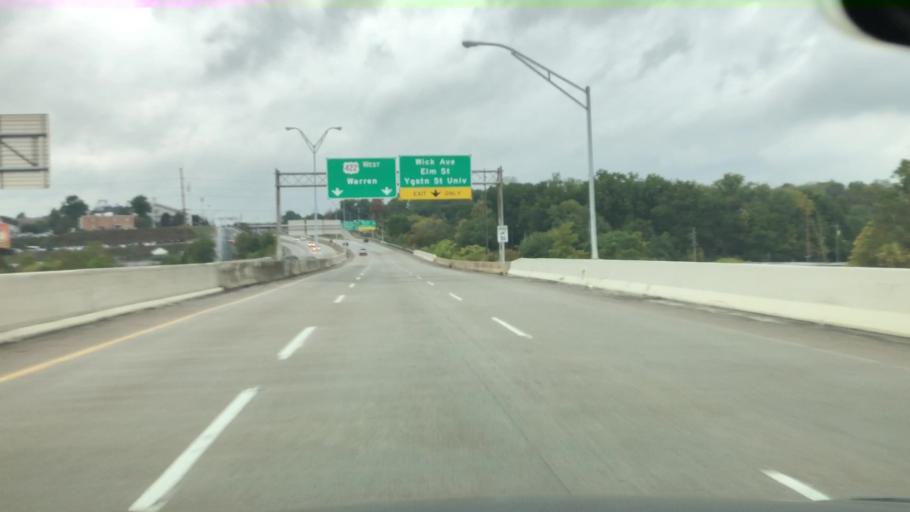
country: US
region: Ohio
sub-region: Mahoning County
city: Youngstown
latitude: 41.1049
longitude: -80.6369
